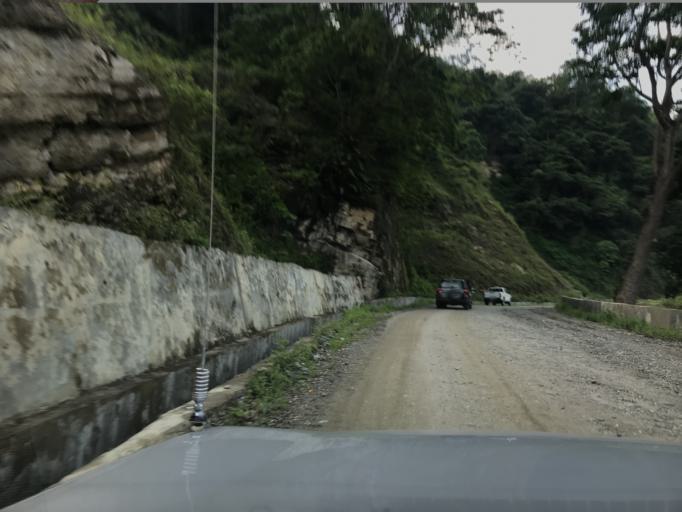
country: TL
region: Dili
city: Dili
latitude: -8.6349
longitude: 125.5148
